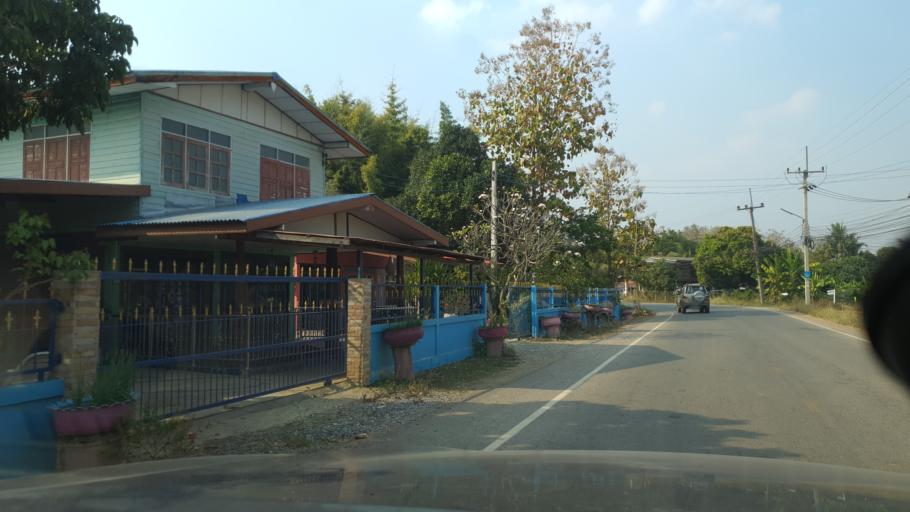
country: TH
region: Sukhothai
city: Ban Dan Lan Hoi
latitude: 17.1156
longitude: 99.5387
